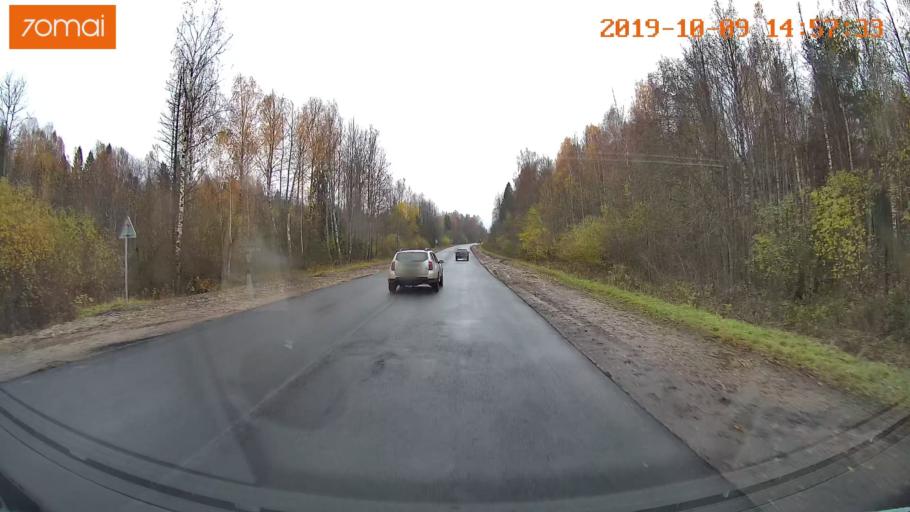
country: RU
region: Kostroma
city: Chistyye Bory
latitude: 58.3365
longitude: 41.6513
